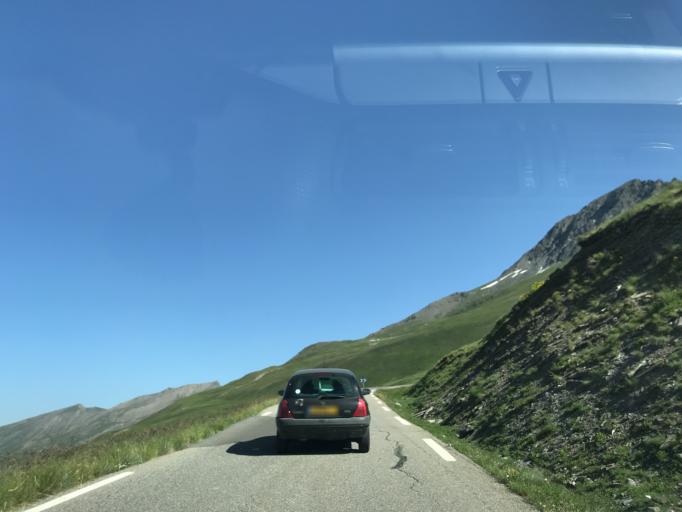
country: IT
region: Piedmont
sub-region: Provincia di Cuneo
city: Pontechianale
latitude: 44.6978
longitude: 6.9495
